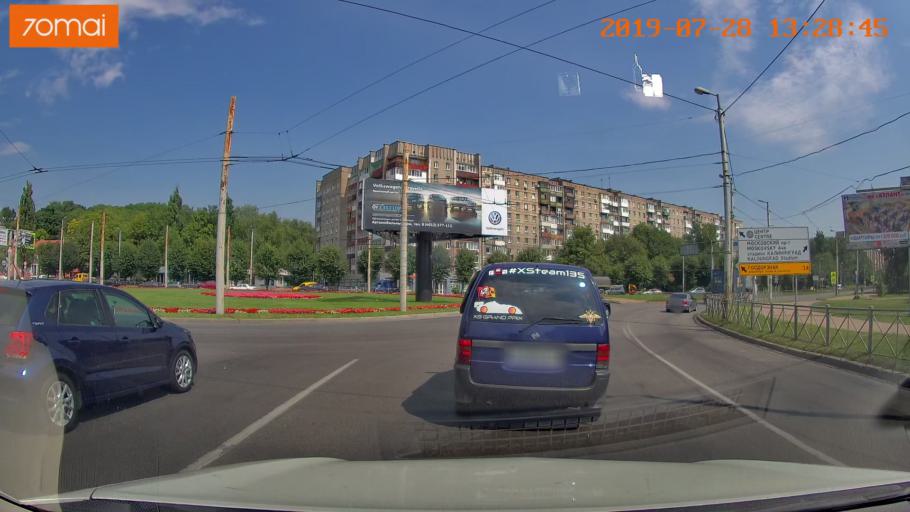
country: RU
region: Kaliningrad
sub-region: Gorod Kaliningrad
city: Kaliningrad
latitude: 54.7089
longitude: 20.5010
